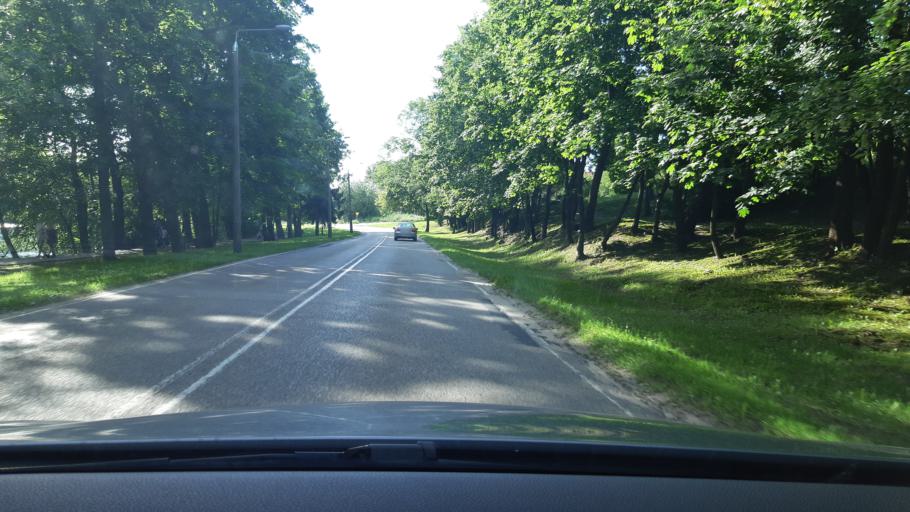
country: PL
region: Warmian-Masurian Voivodeship
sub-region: Powiat mragowski
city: Mragowo
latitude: 53.8766
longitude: 21.3106
